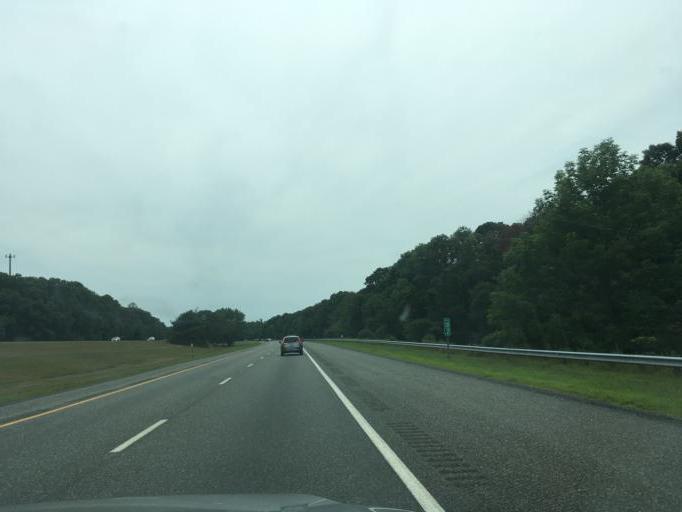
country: US
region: Rhode Island
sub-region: Washington County
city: Hope Valley
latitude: 41.5518
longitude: -71.6728
